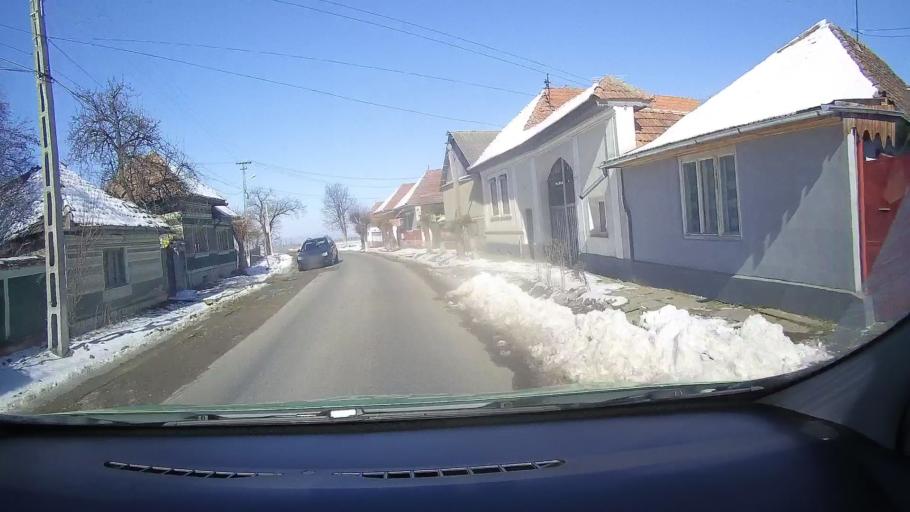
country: RO
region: Brasov
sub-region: Comuna Harseni
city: Harseni
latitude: 45.7587
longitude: 25.0095
